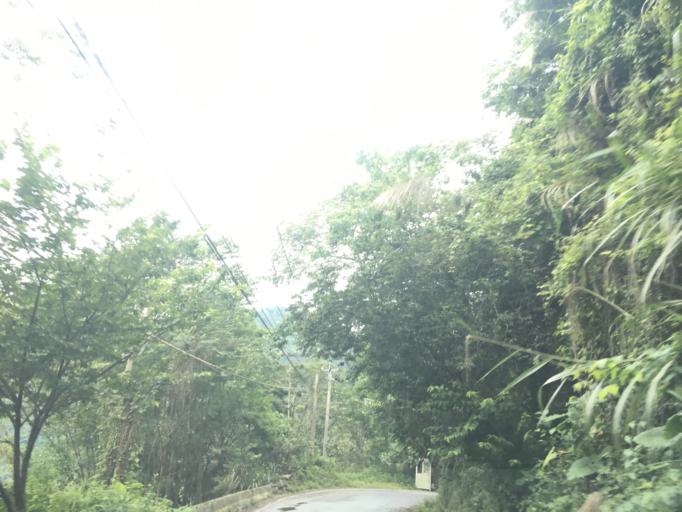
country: TW
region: Taiwan
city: Lugu
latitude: 23.5393
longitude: 120.7147
